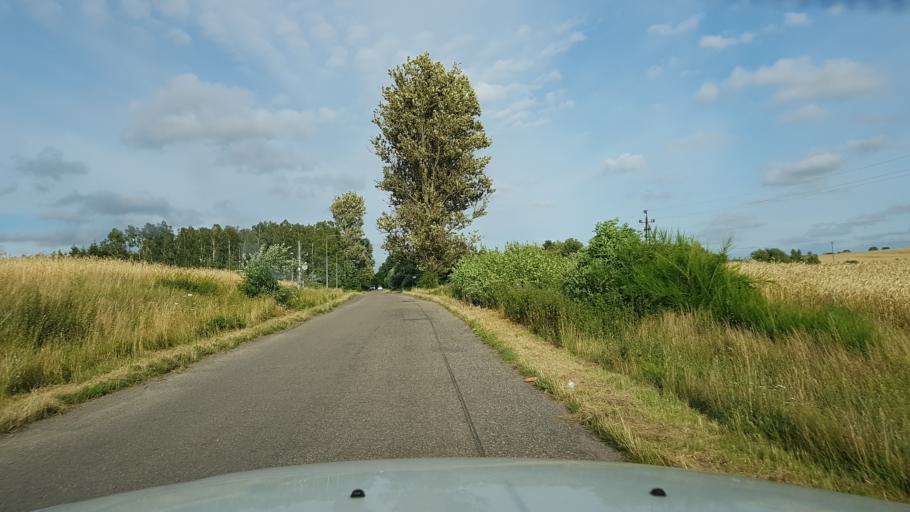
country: PL
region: West Pomeranian Voivodeship
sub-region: Powiat kolobrzeski
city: Kolobrzeg
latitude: 54.0890
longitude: 15.5549
